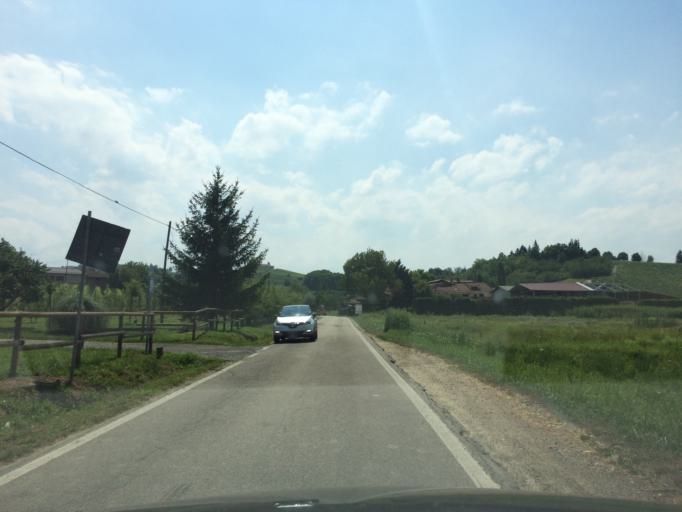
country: IT
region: Piedmont
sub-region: Provincia di Asti
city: San Marzano Oliveto
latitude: 44.7686
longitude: 8.3099
